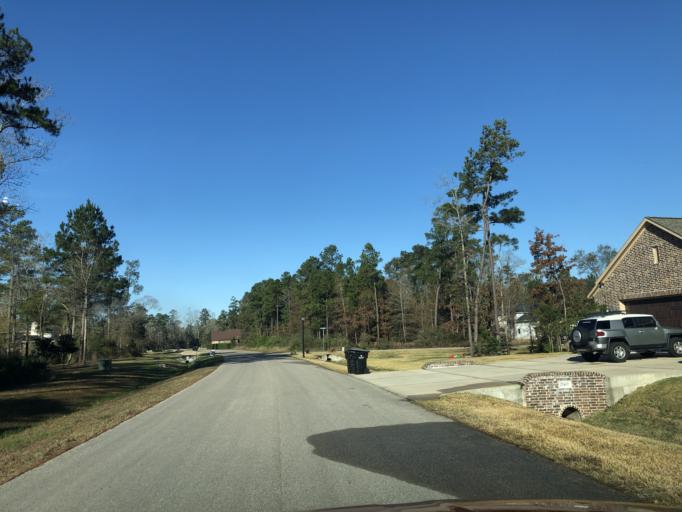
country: US
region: Texas
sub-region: Montgomery County
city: Porter Heights
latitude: 30.0680
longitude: -95.3248
